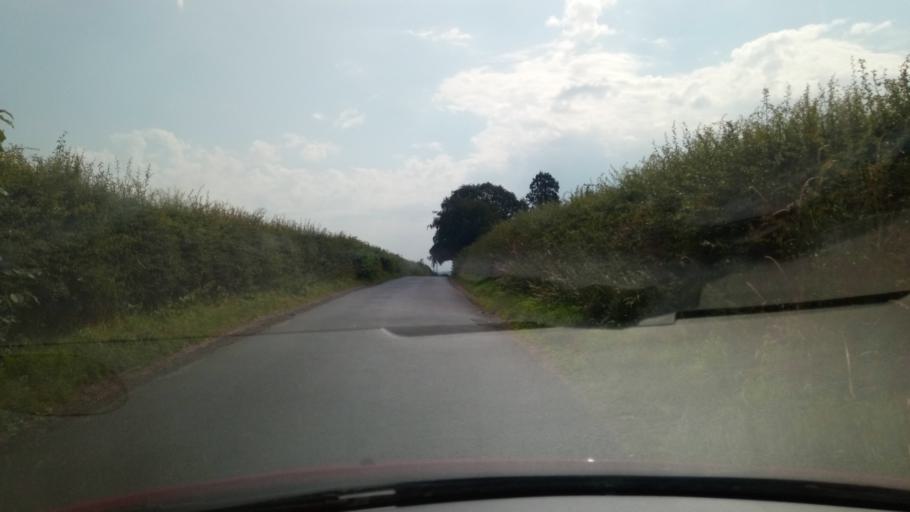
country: GB
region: Scotland
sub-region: The Scottish Borders
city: Kelso
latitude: 55.5809
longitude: -2.4733
